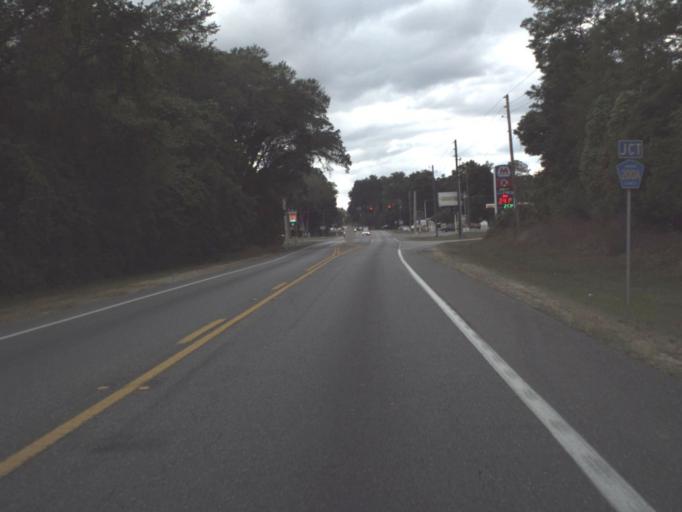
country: US
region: Florida
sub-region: Marion County
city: Ocala
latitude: 29.2595
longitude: -82.1115
